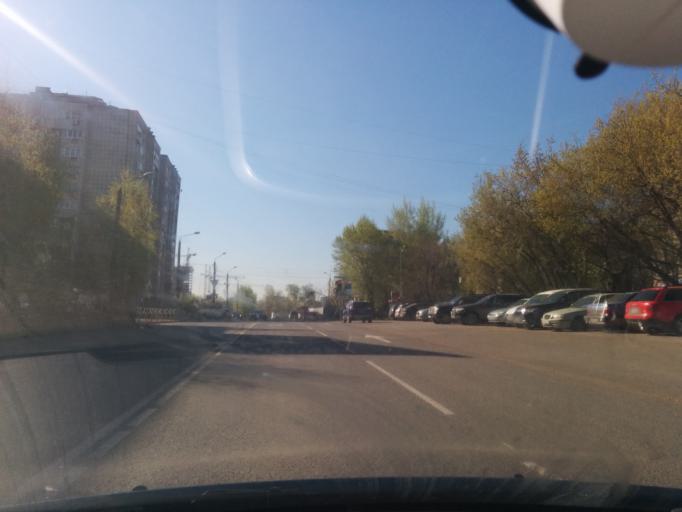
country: RU
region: Perm
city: Perm
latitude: 58.0035
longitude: 56.2149
